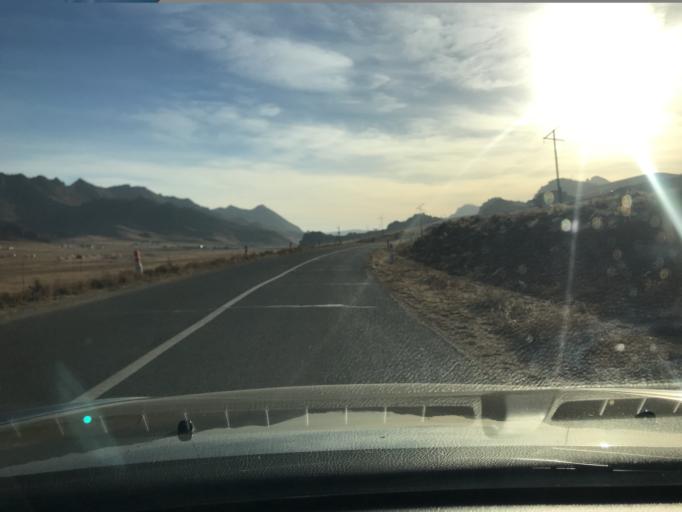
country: MN
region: Central Aimak
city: Arhust
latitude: 47.8753
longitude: 107.4350
